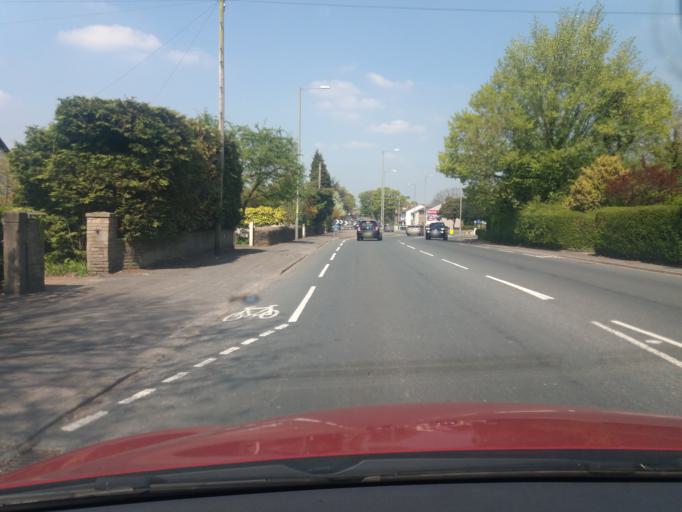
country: GB
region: England
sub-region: Lancashire
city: Chorley
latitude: 53.6769
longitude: -2.6353
